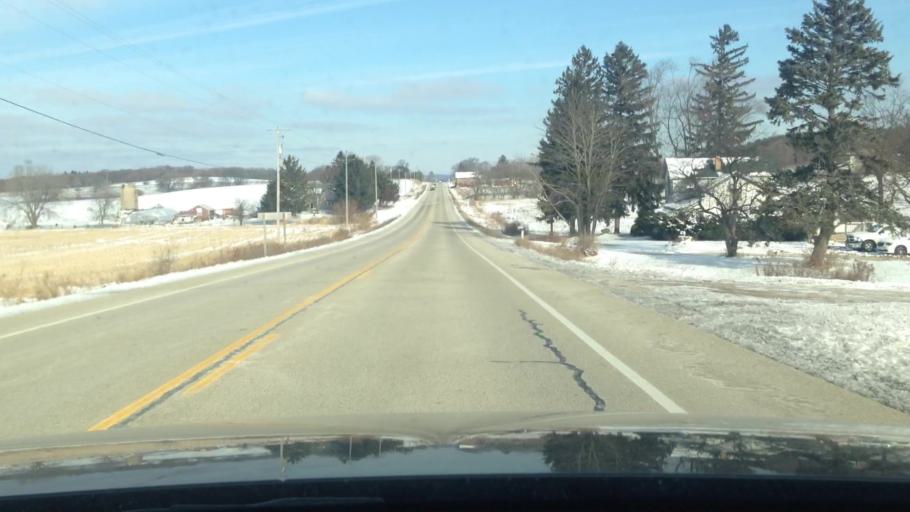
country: US
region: Wisconsin
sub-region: Walworth County
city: East Troy
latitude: 42.7606
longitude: -88.4065
